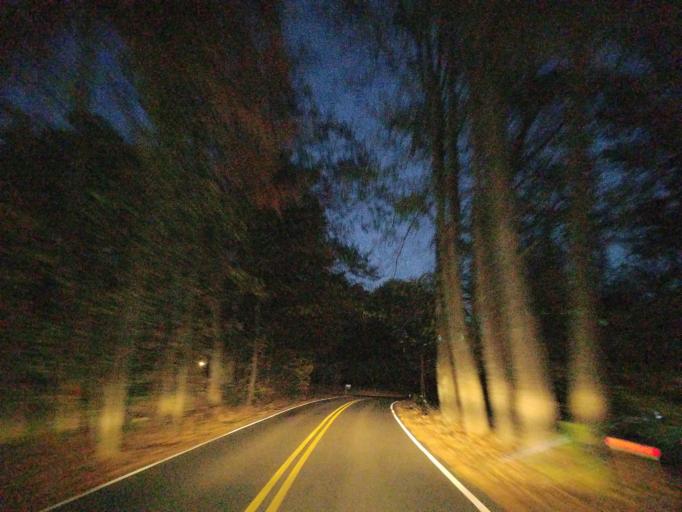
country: US
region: Georgia
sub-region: Forsyth County
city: Cumming
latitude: 34.2561
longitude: -84.1038
